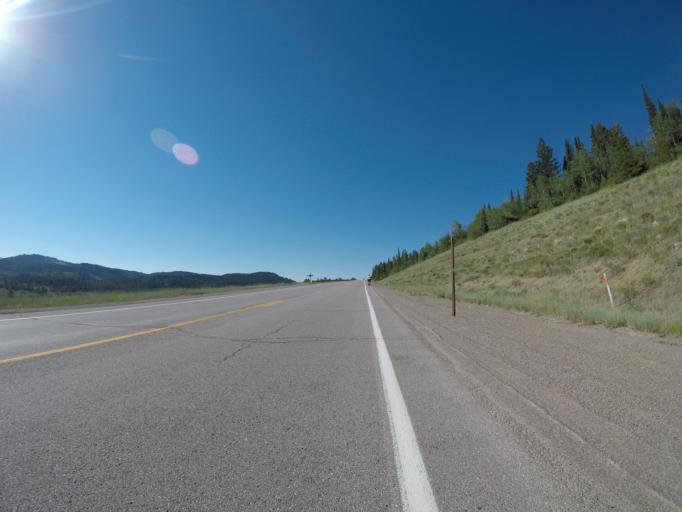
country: US
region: Wyoming
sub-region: Lincoln County
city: Afton
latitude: 42.5115
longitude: -110.9096
